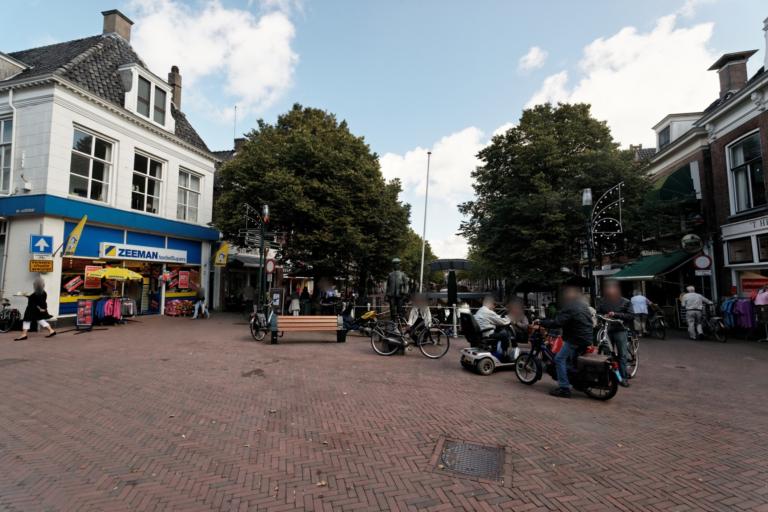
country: NL
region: Friesland
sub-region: Gemeente Harlingen
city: Harlingen
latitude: 53.1746
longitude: 5.4196
